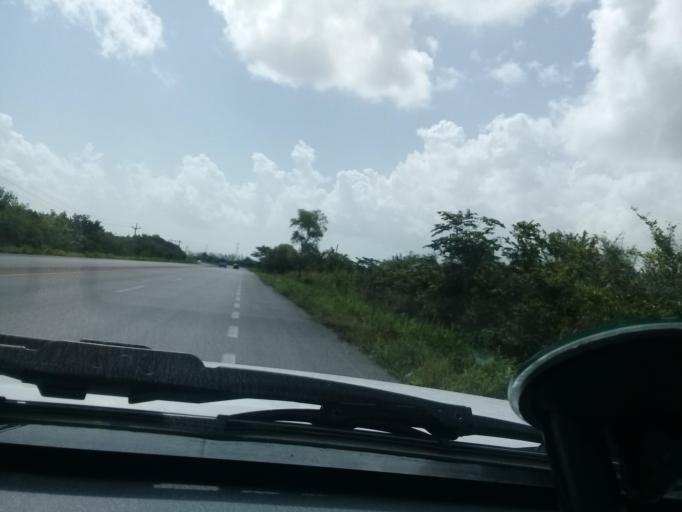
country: MX
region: Veracruz
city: Moralillo
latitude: 22.2122
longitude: -97.9666
